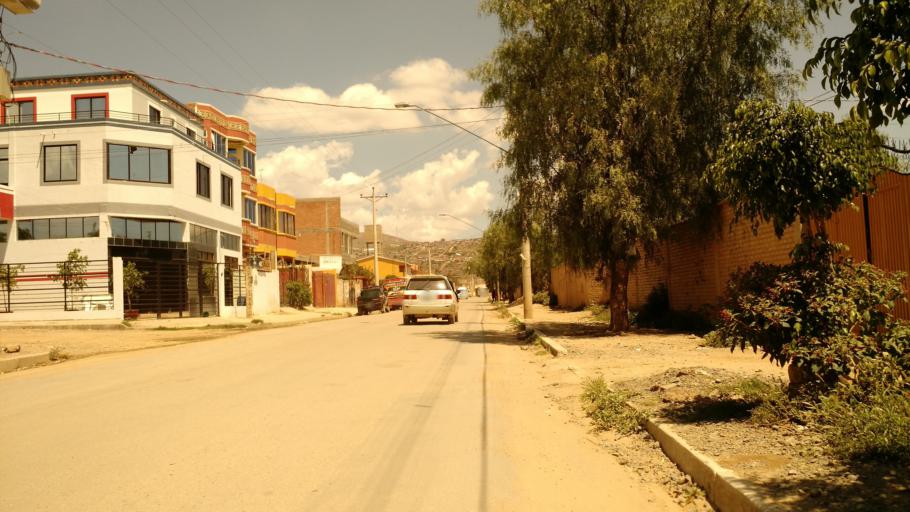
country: BO
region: Cochabamba
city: Cochabamba
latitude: -17.4496
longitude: -66.1557
